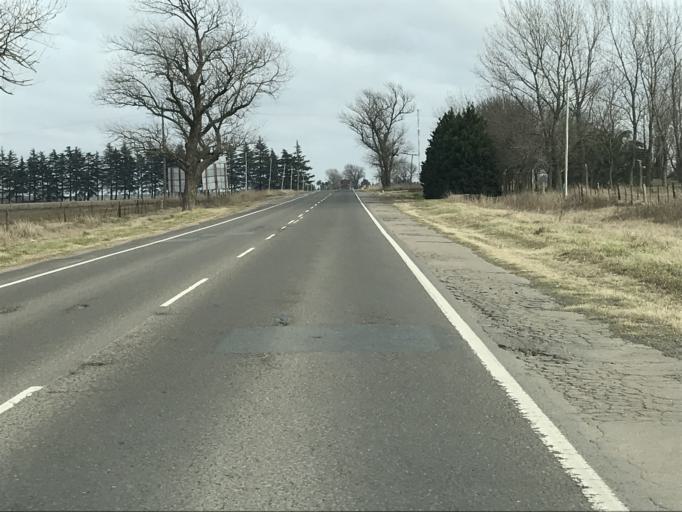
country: AR
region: Santa Fe
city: Canada de Gomez
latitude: -32.8009
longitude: -61.4485
